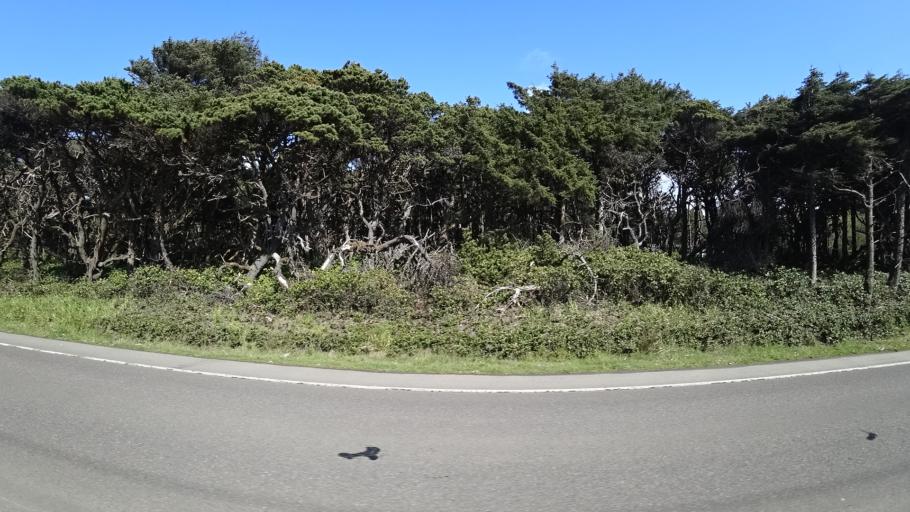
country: US
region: Oregon
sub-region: Lincoln County
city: Newport
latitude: 44.5545
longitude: -124.0718
